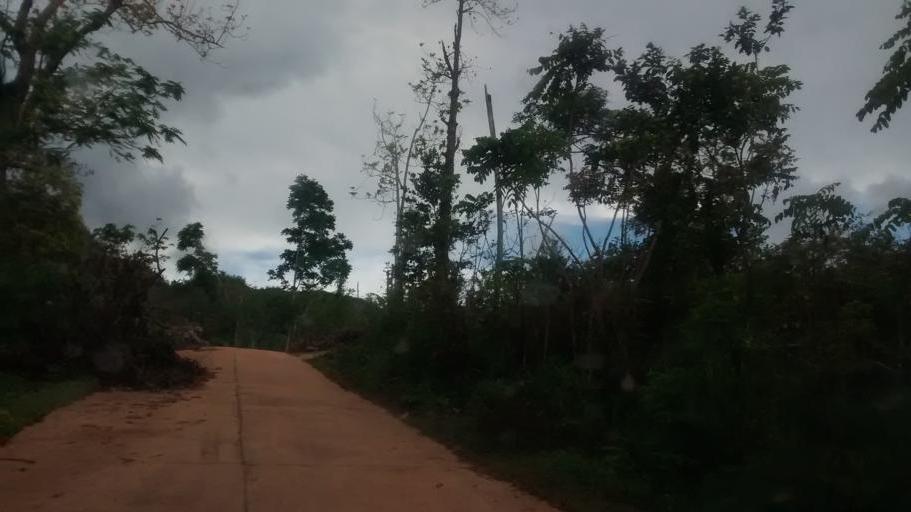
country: HT
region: Grandans
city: Corail
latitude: 18.5176
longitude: -73.7871
